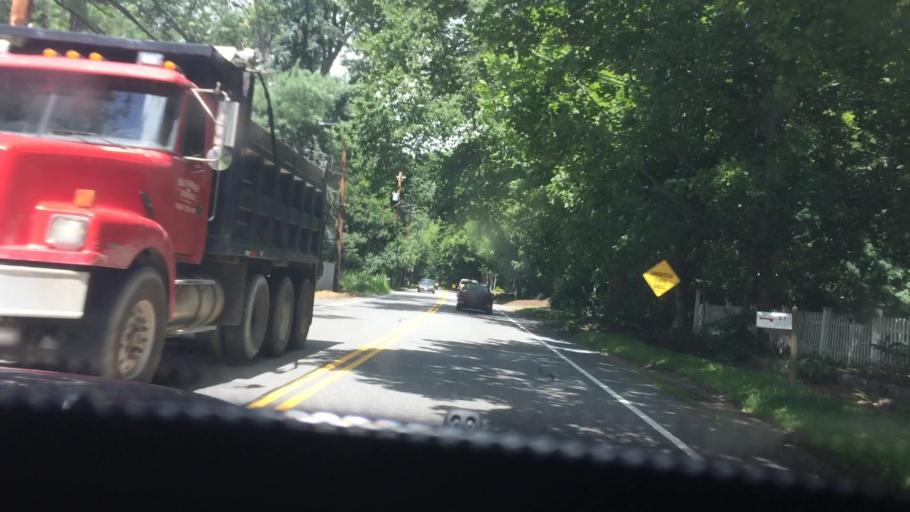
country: US
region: Massachusetts
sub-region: Middlesex County
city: Wayland
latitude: 42.3728
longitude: -71.3716
